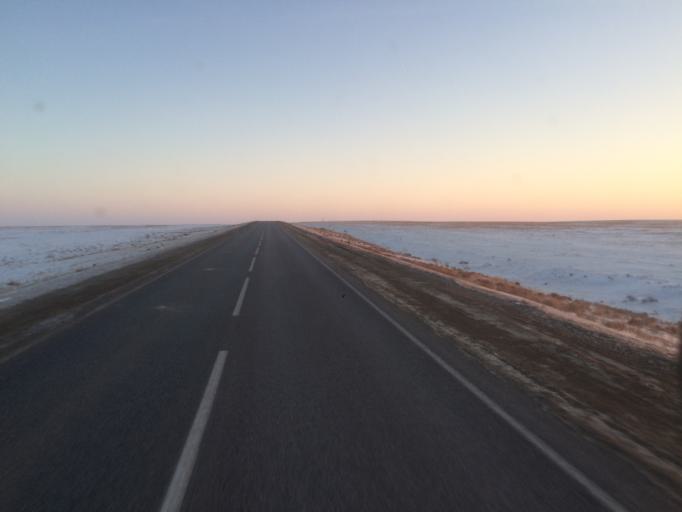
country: KZ
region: Qyzylorda
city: Sekseuil
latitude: 47.5717
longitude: 61.5114
